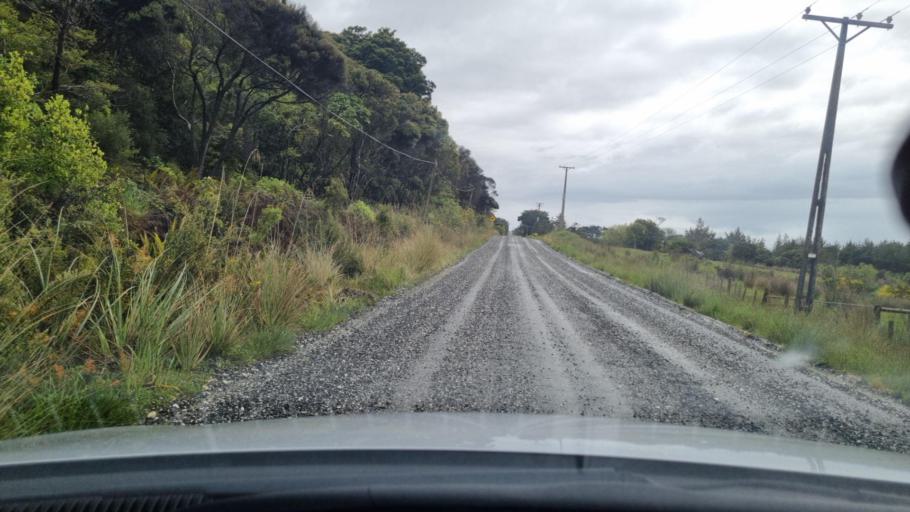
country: NZ
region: Southland
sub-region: Invercargill City
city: Bluff
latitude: -46.5370
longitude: 168.2653
